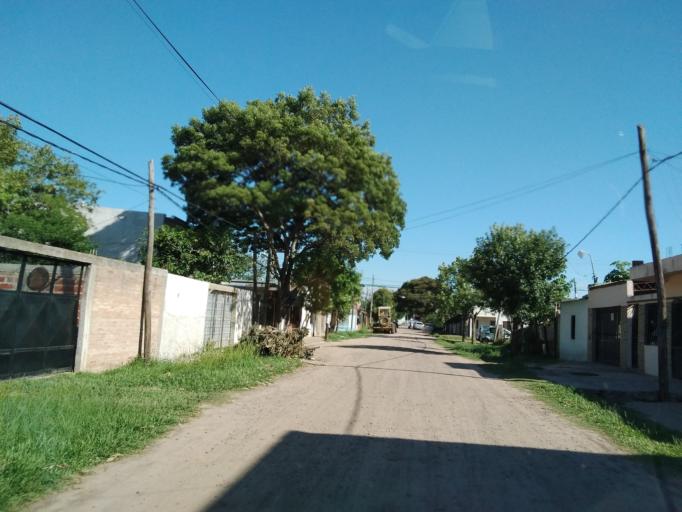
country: AR
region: Corrientes
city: Corrientes
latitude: -27.4854
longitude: -58.8036
